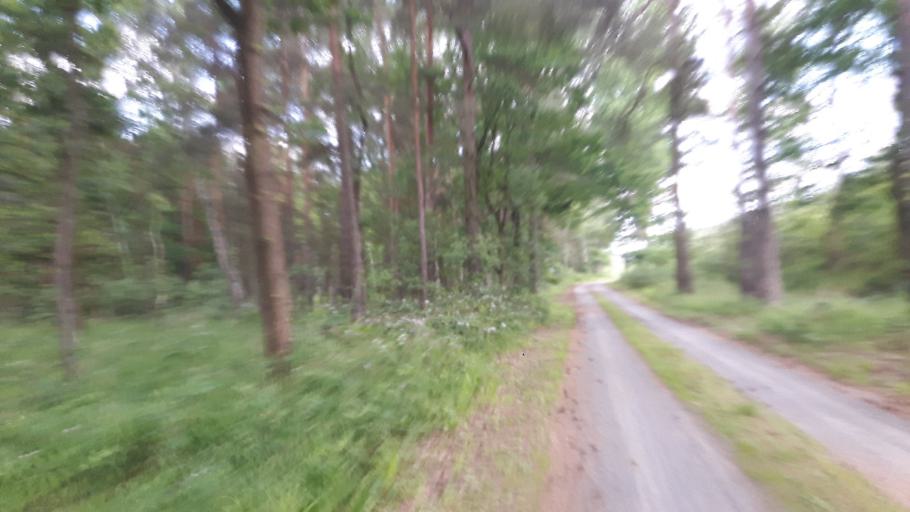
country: DE
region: Saxony-Anhalt
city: Bergwitz
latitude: 51.7841
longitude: 12.5470
